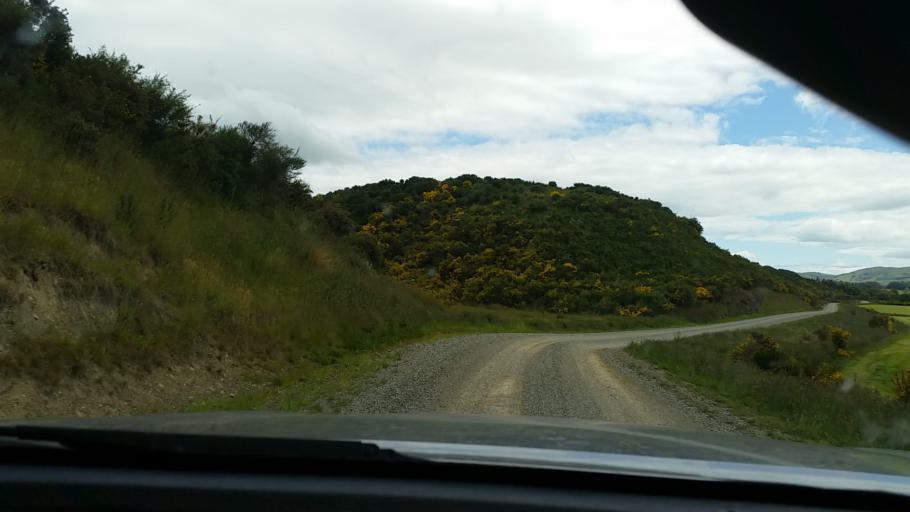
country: NZ
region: Otago
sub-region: Queenstown-Lakes District
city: Kingston
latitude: -45.7531
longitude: 168.5939
